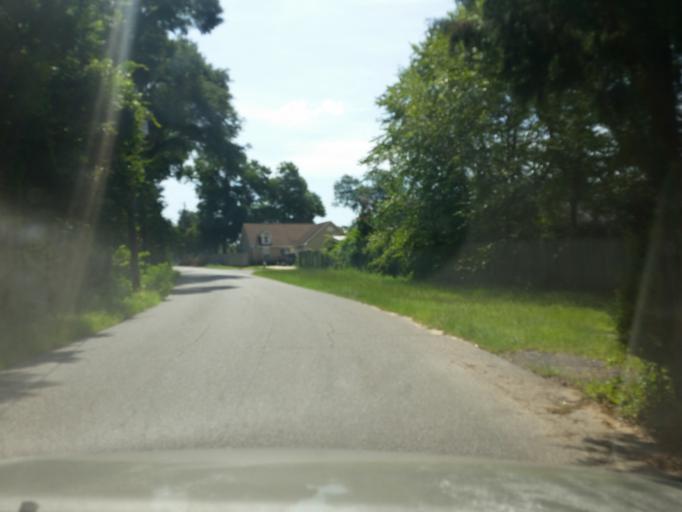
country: US
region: Florida
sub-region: Escambia County
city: Ferry Pass
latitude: 30.5145
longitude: -87.2014
